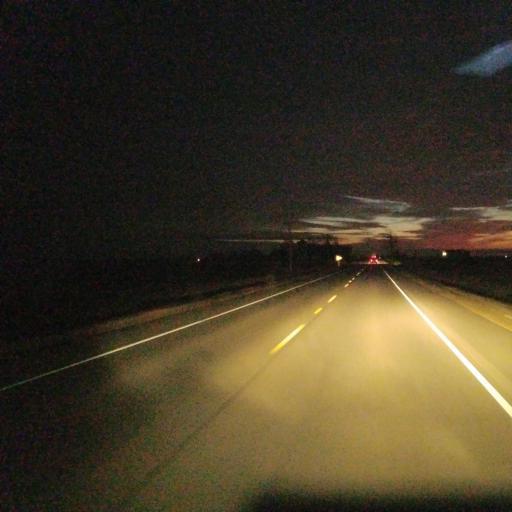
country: US
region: Illinois
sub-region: Fulton County
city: Farmington
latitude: 40.6982
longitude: -89.9383
